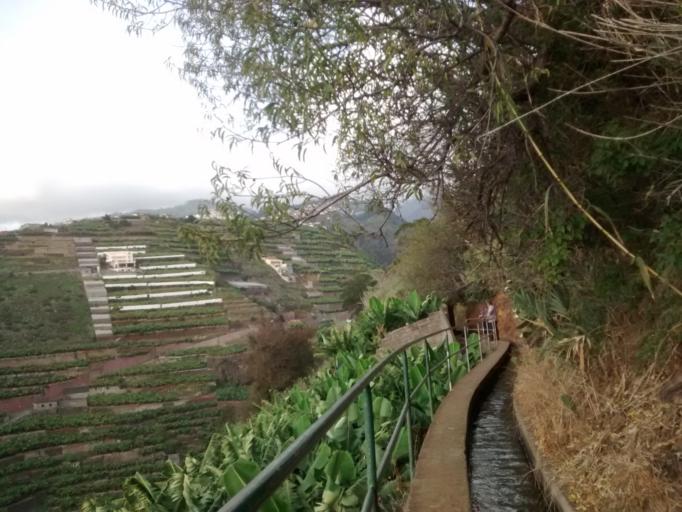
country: PT
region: Madeira
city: Camara de Lobos
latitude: 32.6548
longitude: -16.9626
